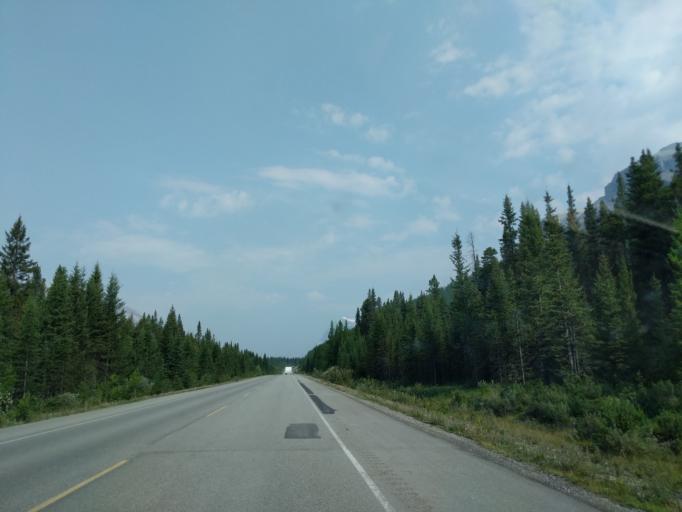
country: CA
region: Alberta
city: Lake Louise
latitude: 51.8766
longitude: -116.6786
